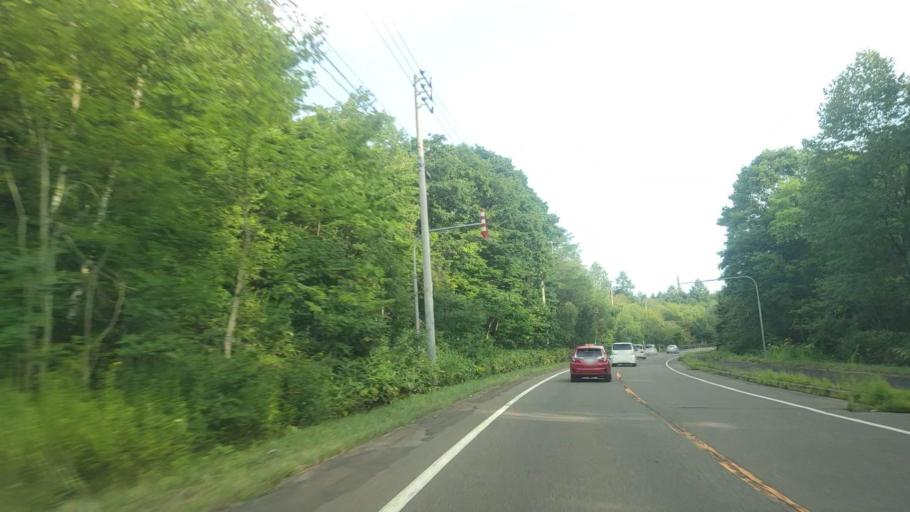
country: JP
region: Hokkaido
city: Iwamizawa
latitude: 43.0331
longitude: 141.9415
